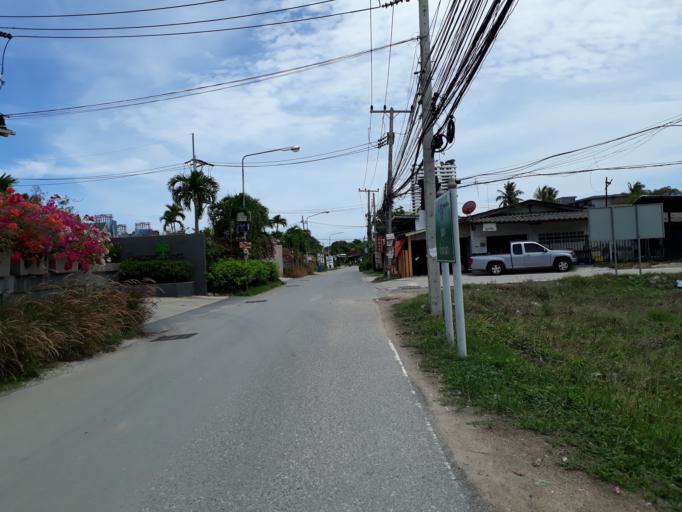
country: TH
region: Chon Buri
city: Phatthaya
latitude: 12.8447
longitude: 100.9088
